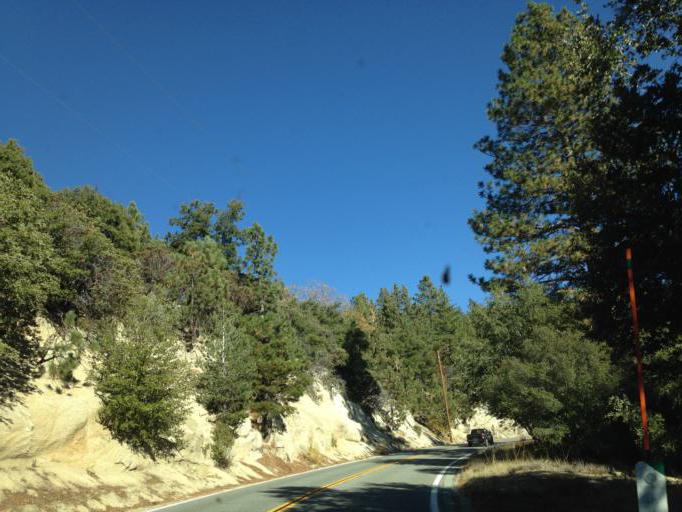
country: US
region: California
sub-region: Riverside County
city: Idyllwild-Pine Cove
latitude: 33.7793
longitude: -116.7420
